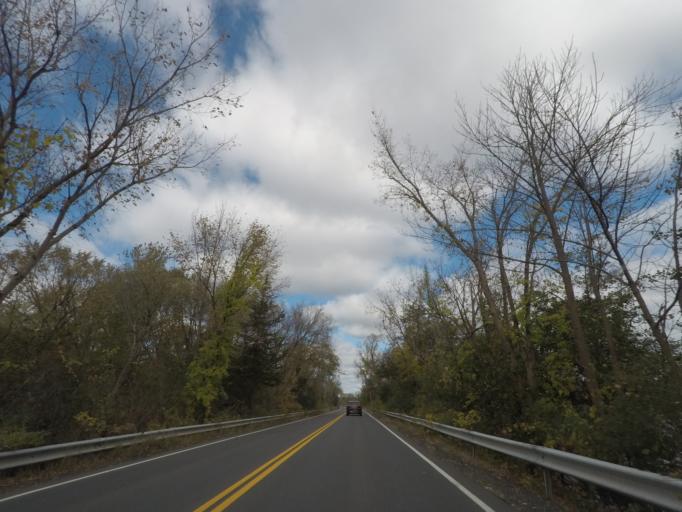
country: US
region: New York
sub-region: Albany County
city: Cohoes
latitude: 42.8065
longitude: -73.7246
